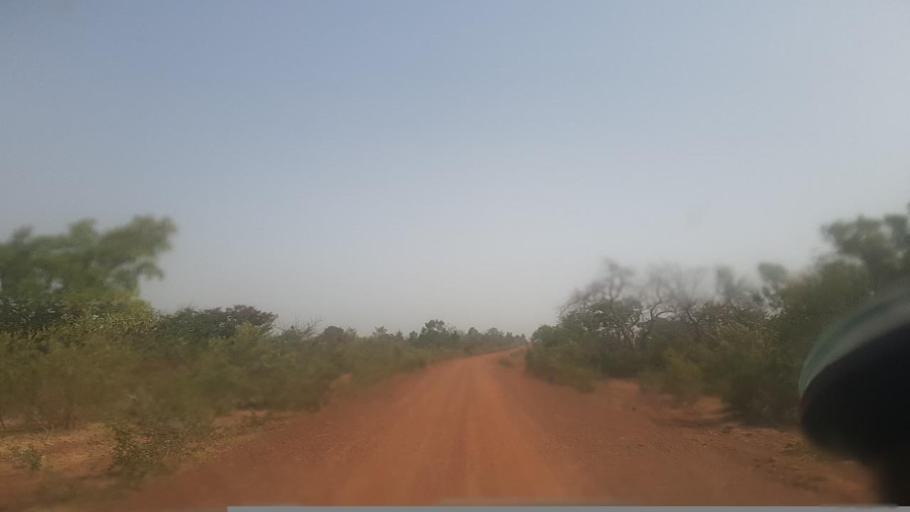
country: ML
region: Segou
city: Segou
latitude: 12.9306
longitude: -6.2819
